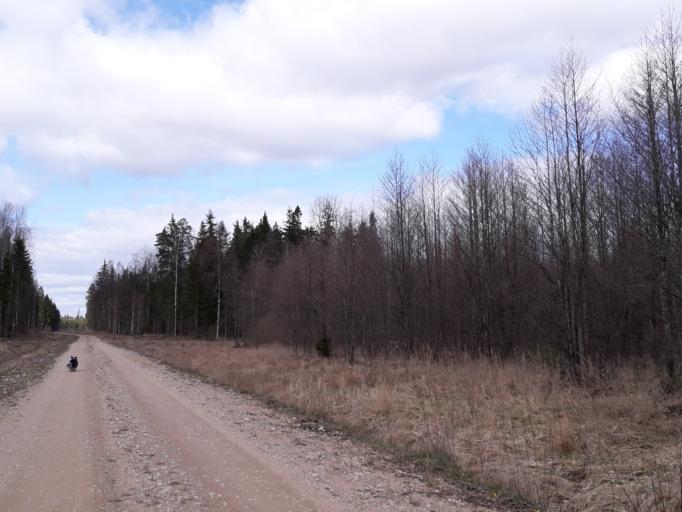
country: LV
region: Talsu Rajons
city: Sabile
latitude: 56.9010
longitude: 22.3772
